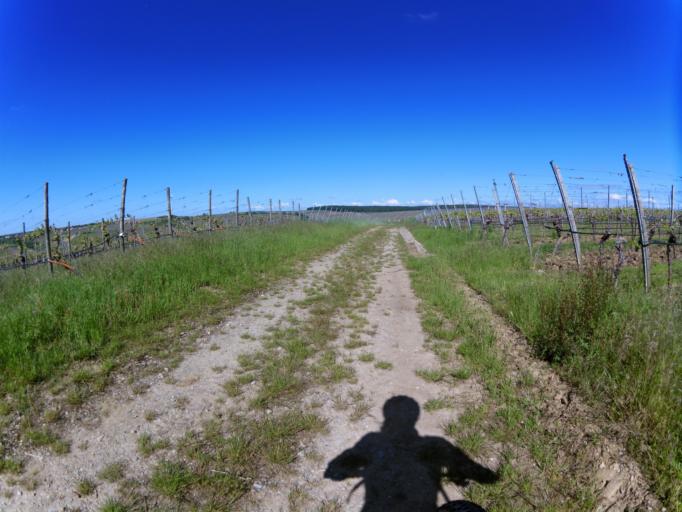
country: DE
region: Bavaria
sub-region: Regierungsbezirk Unterfranken
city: Sommerach
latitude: 49.8383
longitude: 10.1950
